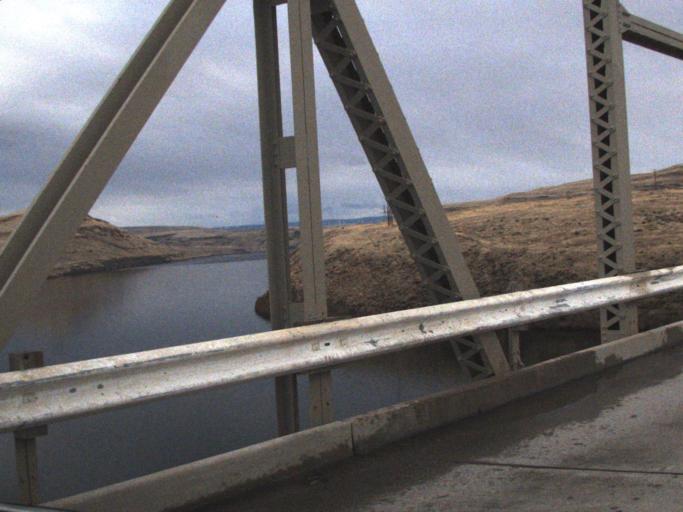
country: US
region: Washington
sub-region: Walla Walla County
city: Waitsburg
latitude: 46.5890
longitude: -118.2194
